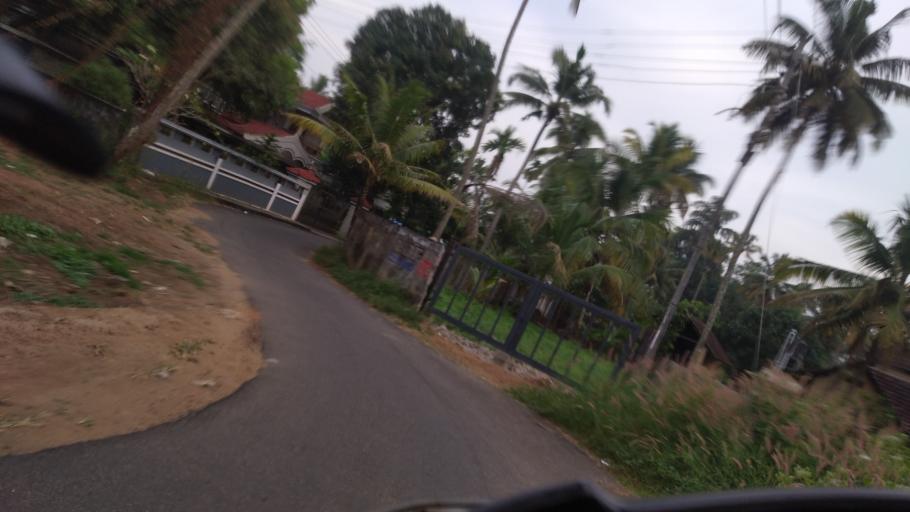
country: IN
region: Kerala
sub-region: Thrissur District
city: Kodungallur
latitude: 10.1383
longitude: 76.2000
